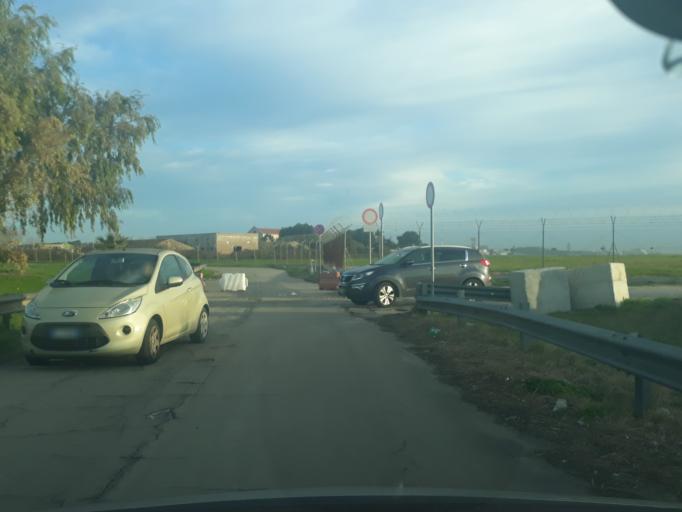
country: IT
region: Apulia
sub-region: Provincia di Brindisi
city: Brindisi
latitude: 40.6507
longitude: 17.9334
